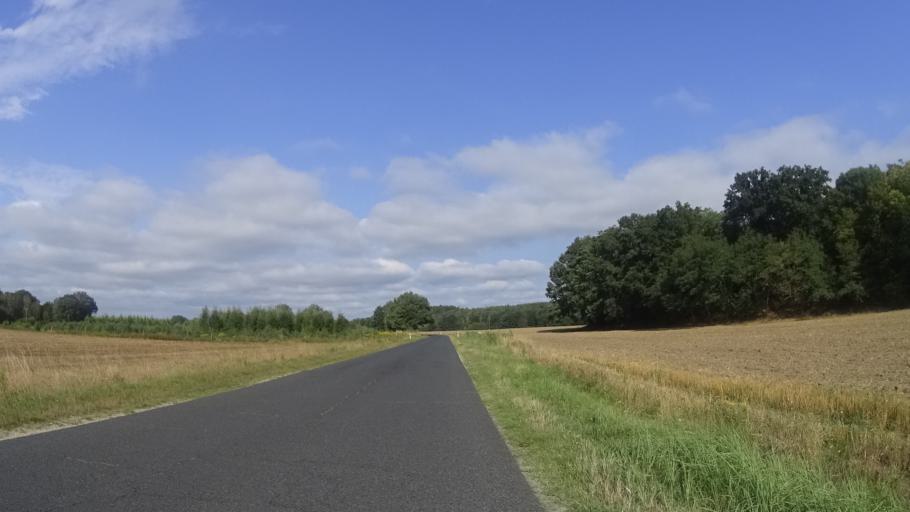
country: PL
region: Lubusz
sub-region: Powiat zarski
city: Przewoz
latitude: 51.4858
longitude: 14.9151
